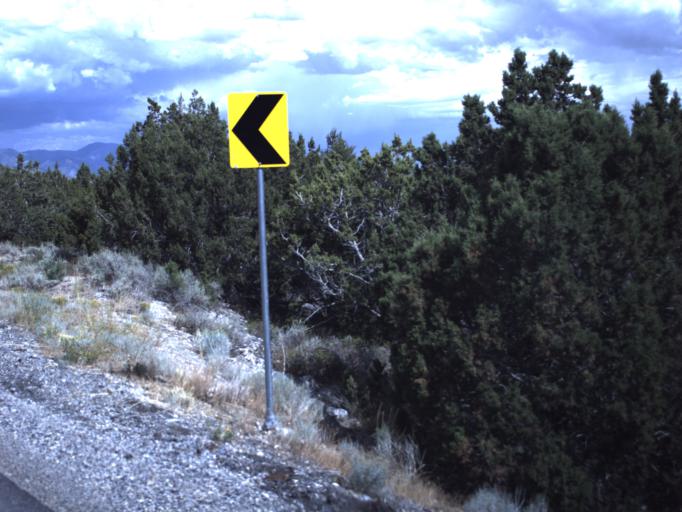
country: US
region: Utah
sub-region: Tooele County
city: Grantsville
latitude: 40.3485
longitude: -112.5587
